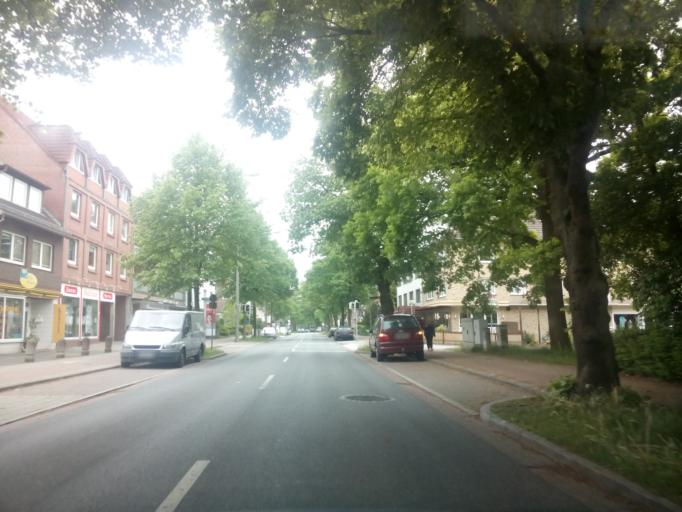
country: DE
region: Lower Saxony
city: Schwanewede
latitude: 53.2028
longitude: 8.5757
